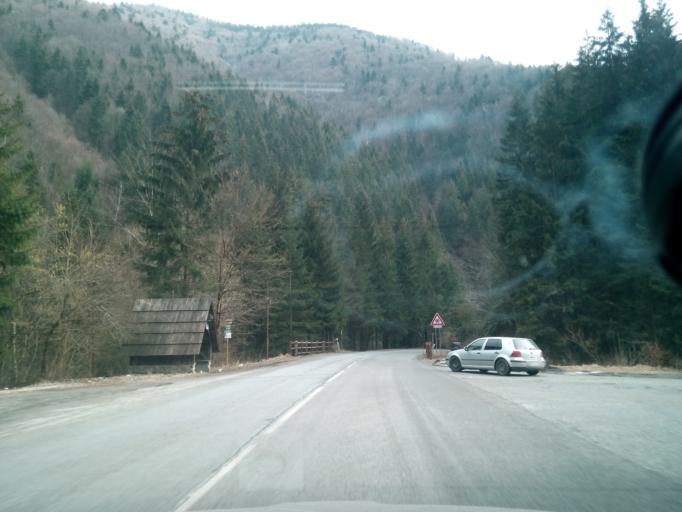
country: SK
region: Zilinsky
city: Oravska Lesna
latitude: 49.2470
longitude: 19.1555
